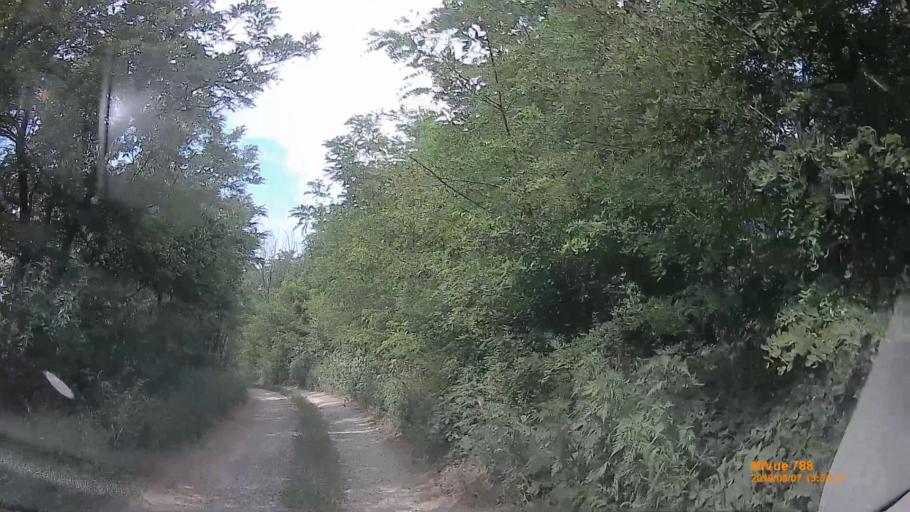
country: HU
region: Zala
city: Cserszegtomaj
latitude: 46.8934
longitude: 17.1791
